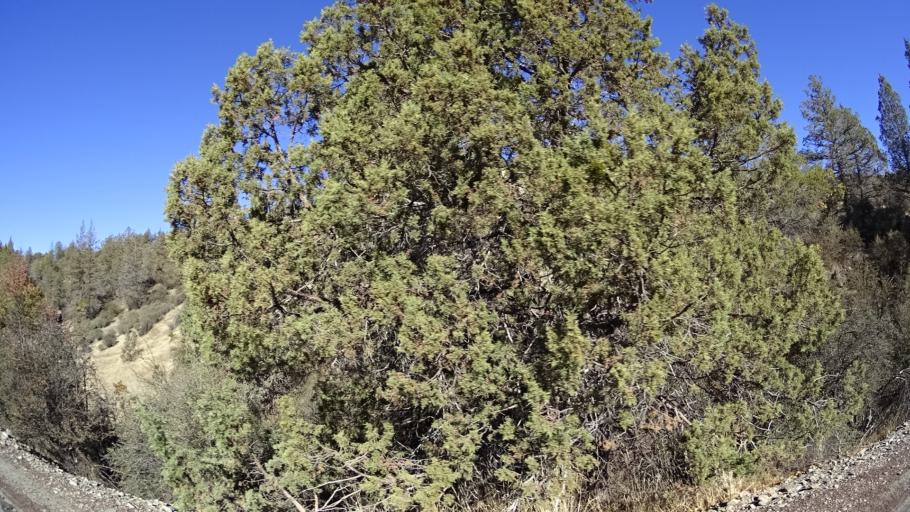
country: US
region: California
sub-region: Siskiyou County
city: Montague
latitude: 41.9567
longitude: -122.3268
